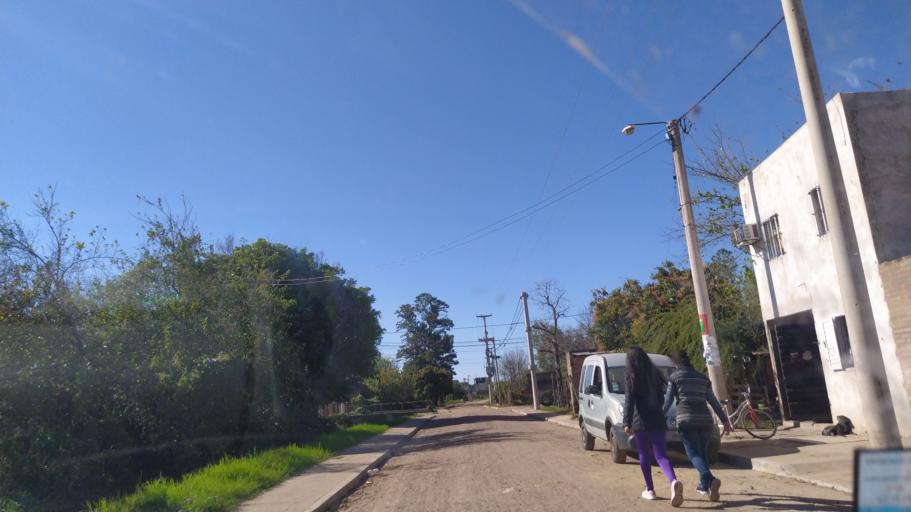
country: AR
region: Corrientes
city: Corrientes
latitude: -27.4981
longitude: -58.8074
